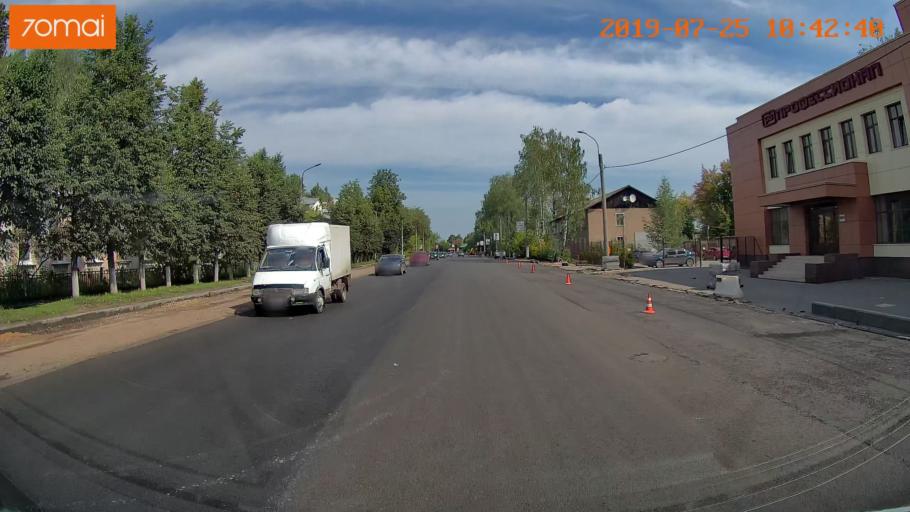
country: RU
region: Ivanovo
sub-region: Gorod Ivanovo
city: Ivanovo
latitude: 57.0303
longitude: 40.9681
